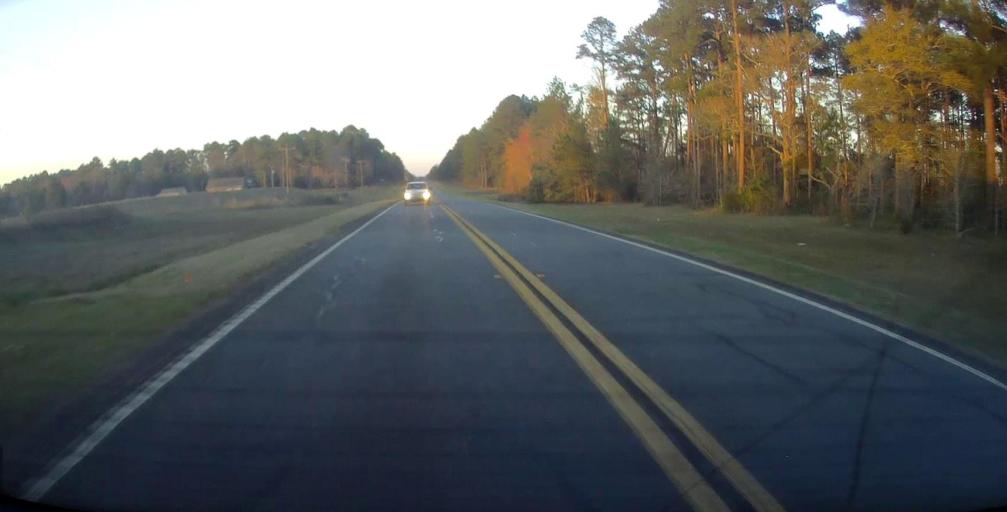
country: US
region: Georgia
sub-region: Dodge County
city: Eastman
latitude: 32.2274
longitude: -83.1535
